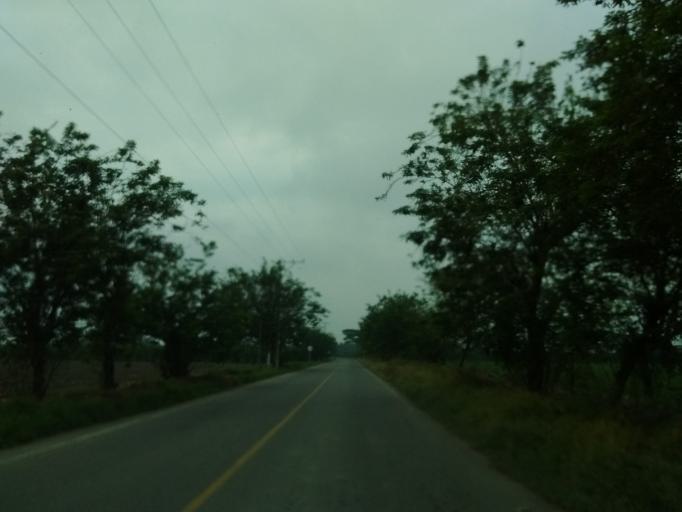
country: CO
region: Cauca
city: Padilla
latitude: 3.2267
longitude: -76.3487
